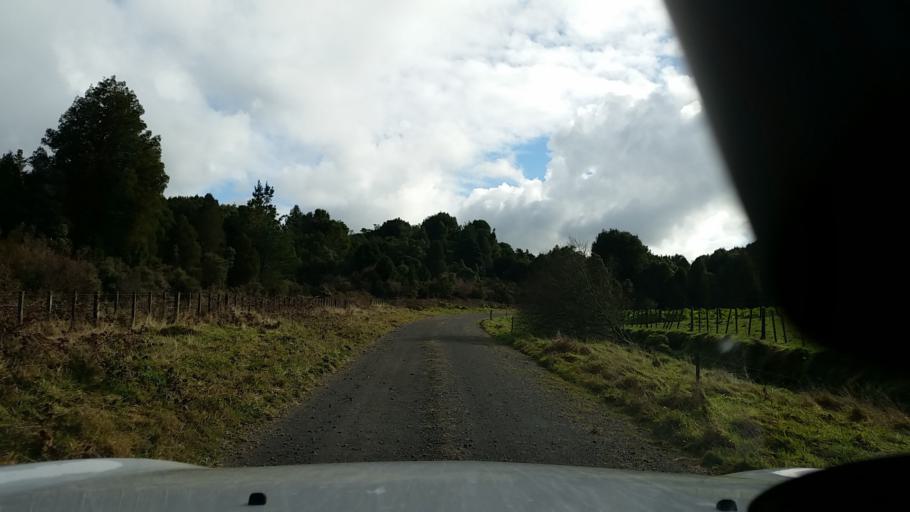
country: NZ
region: Bay of Plenty
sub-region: Rotorua District
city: Rotorua
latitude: -38.0780
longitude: 176.0381
